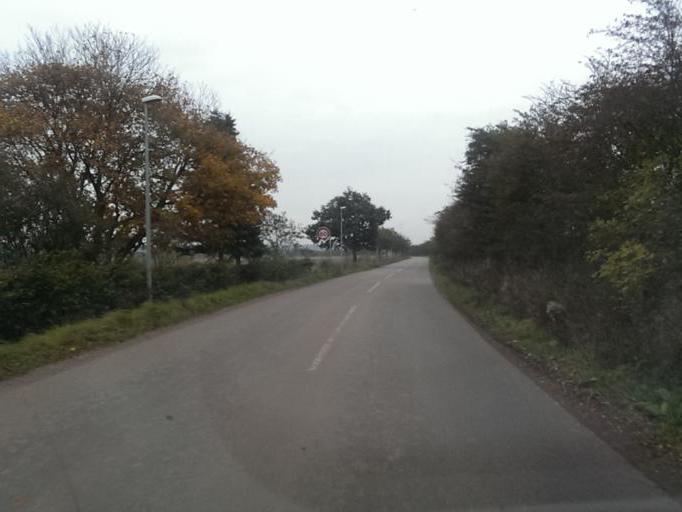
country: DK
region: South Denmark
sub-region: Esbjerg Kommune
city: Tjaereborg
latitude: 55.4948
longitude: 8.5338
